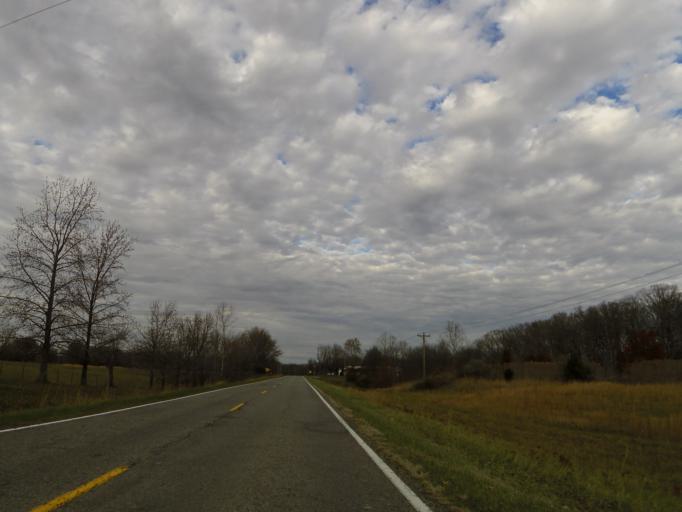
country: US
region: Illinois
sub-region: Jefferson County
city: Mount Vernon
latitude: 38.3681
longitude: -88.9898
